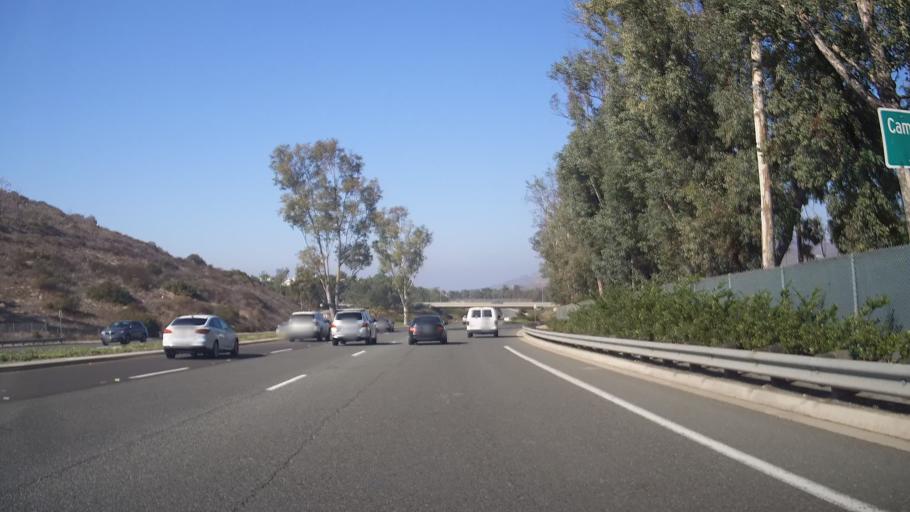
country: US
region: California
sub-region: San Diego County
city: Poway
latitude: 33.0121
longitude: -117.1006
